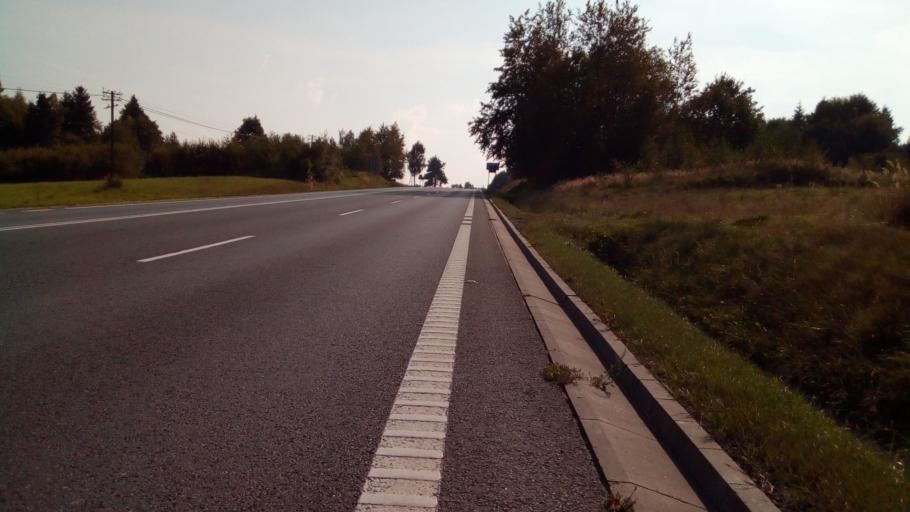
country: PL
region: Subcarpathian Voivodeship
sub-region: Powiat strzyzowski
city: Jawornik
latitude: 49.8416
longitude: 21.8894
